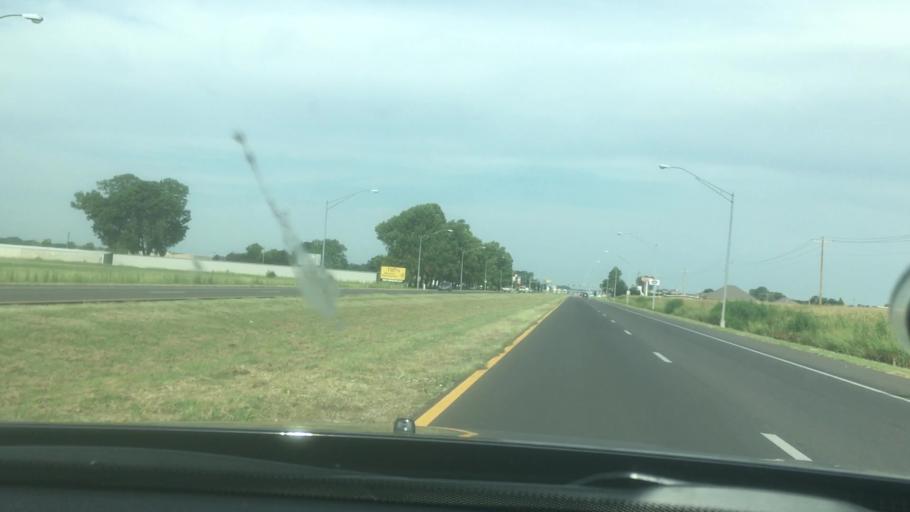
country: US
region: Oklahoma
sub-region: Garvin County
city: Pauls Valley
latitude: 34.7393
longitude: -97.2414
